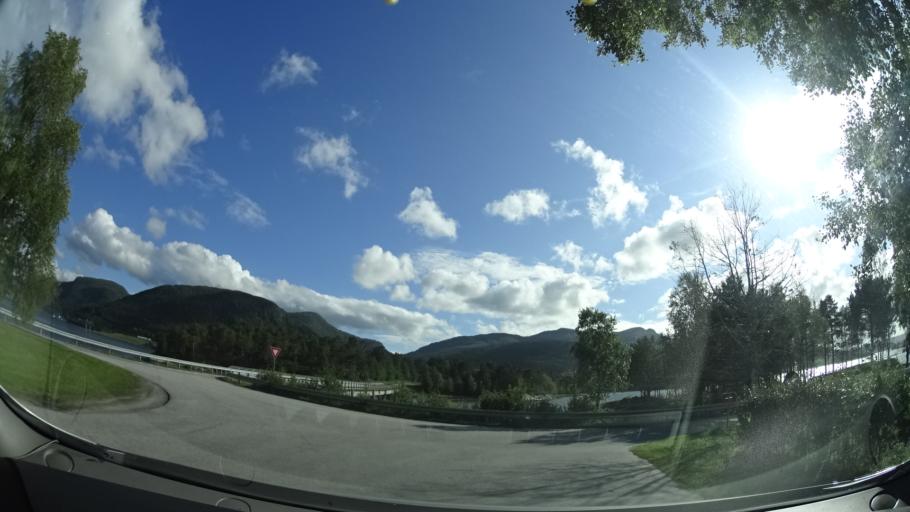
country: NO
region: More og Romsdal
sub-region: Aure
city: Aure
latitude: 63.1417
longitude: 8.5327
